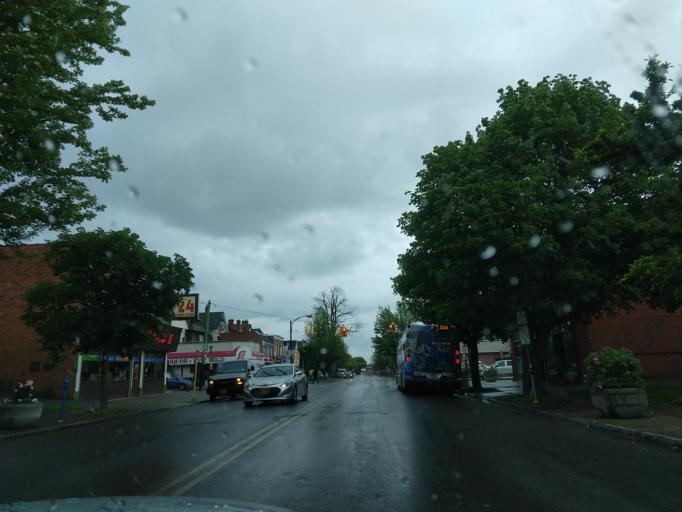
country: US
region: New York
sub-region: Erie County
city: Buffalo
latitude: 42.9257
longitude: -78.8770
